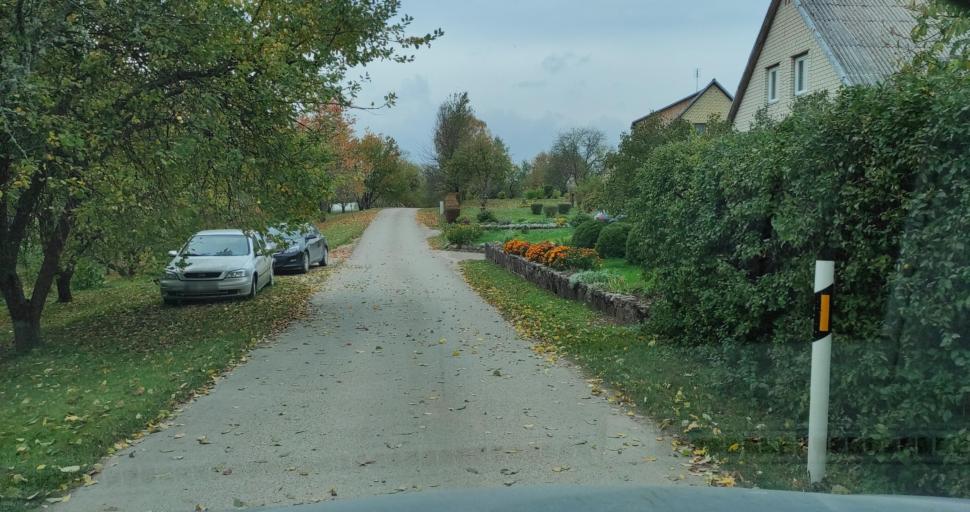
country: LV
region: Alsunga
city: Alsunga
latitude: 57.0197
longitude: 21.6953
